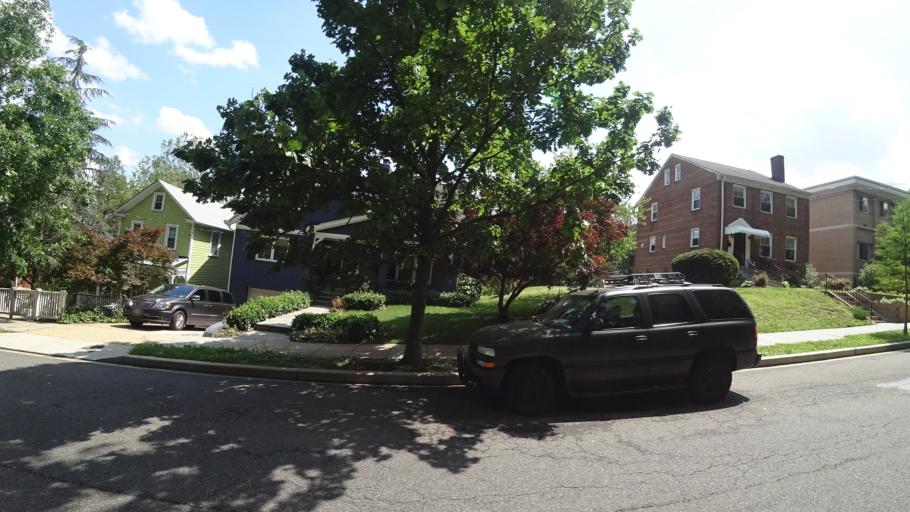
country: US
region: Maryland
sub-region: Prince George's County
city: Mount Rainier
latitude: 38.9347
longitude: -76.9874
